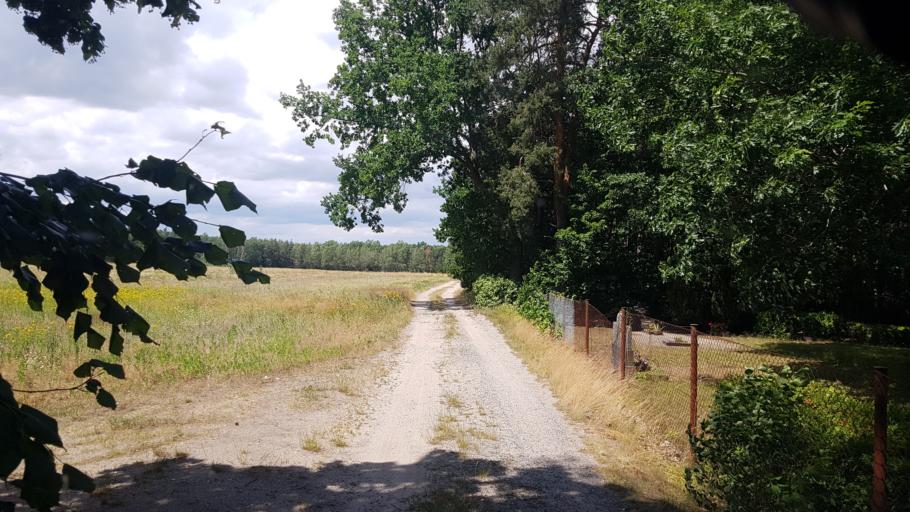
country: DE
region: Brandenburg
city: Sallgast
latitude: 51.5929
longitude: 13.8428
